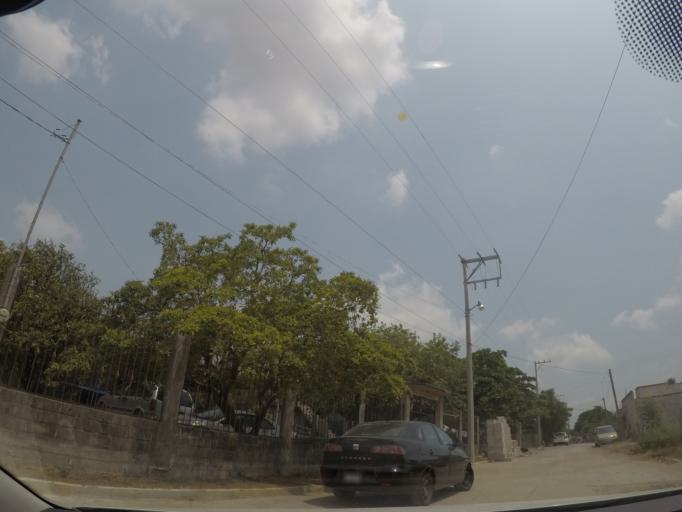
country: MX
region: Oaxaca
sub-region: El Espinal
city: El Espinal
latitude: 16.4764
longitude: -95.0434
